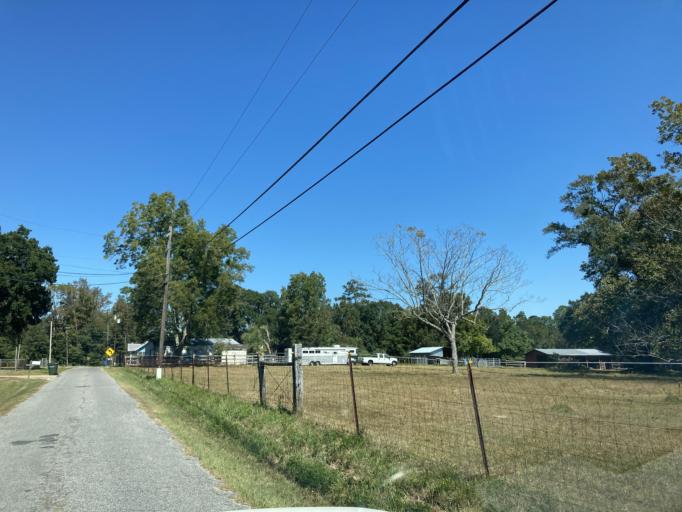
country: US
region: Mississippi
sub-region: Jackson County
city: Saint Martin
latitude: 30.4707
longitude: -88.8750
